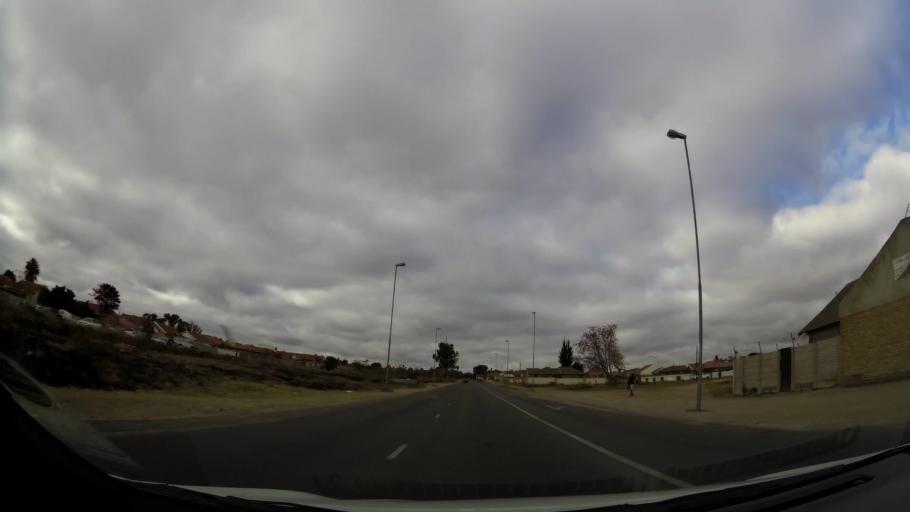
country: ZA
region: Limpopo
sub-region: Capricorn District Municipality
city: Polokwane
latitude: -23.9223
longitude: 29.4478
